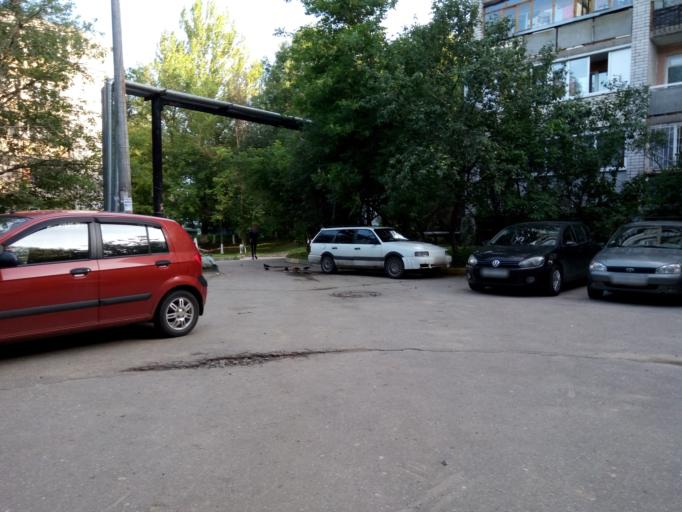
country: RU
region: Nizjnij Novgorod
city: Nizhniy Novgorod
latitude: 56.2719
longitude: 43.9824
